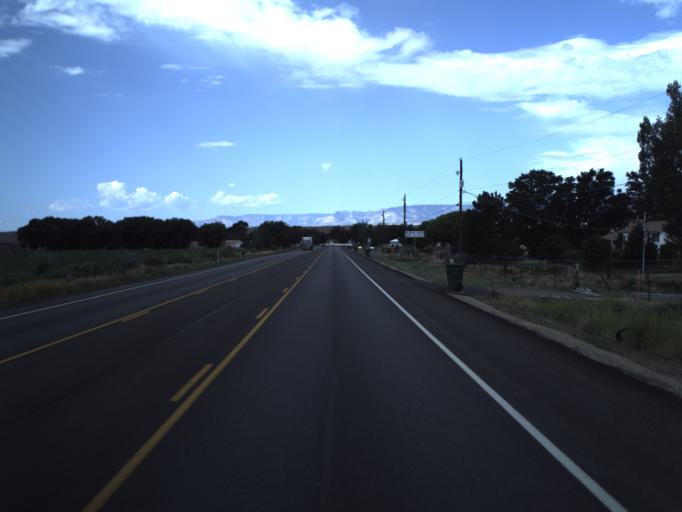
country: US
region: Utah
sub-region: Carbon County
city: Wellington
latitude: 39.5451
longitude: -110.6784
